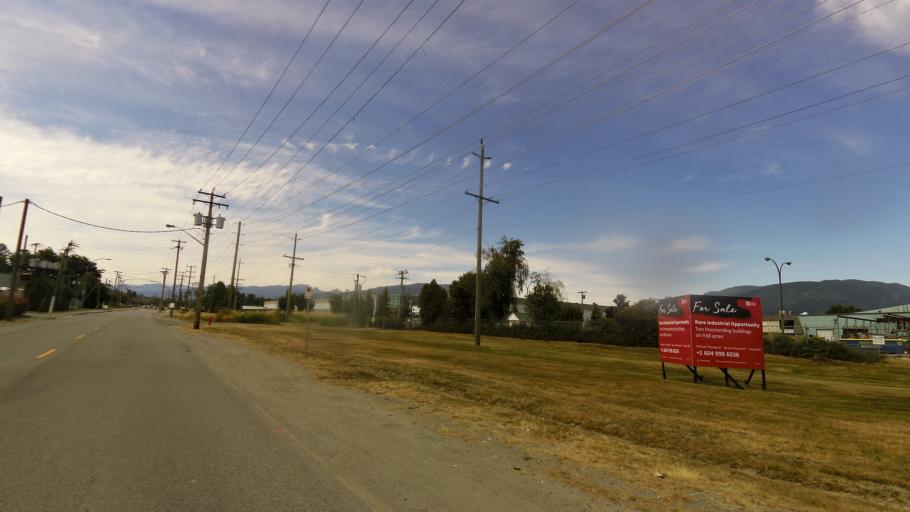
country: CA
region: British Columbia
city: Coquitlam
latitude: 49.2509
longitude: -122.7579
